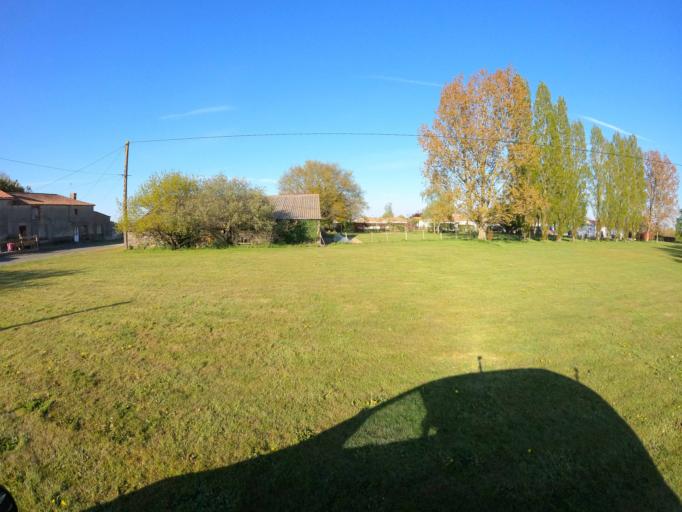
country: FR
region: Pays de la Loire
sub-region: Departement de la Vendee
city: Les Brouzils
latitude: 46.8833
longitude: -1.3337
